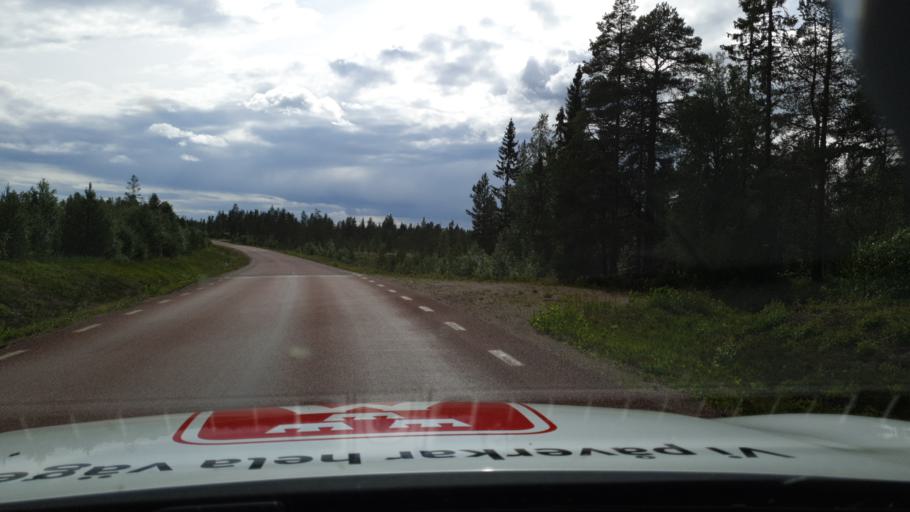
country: SE
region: Dalarna
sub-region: Alvdalens Kommun
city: AElvdalen
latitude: 61.7589
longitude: 13.4566
